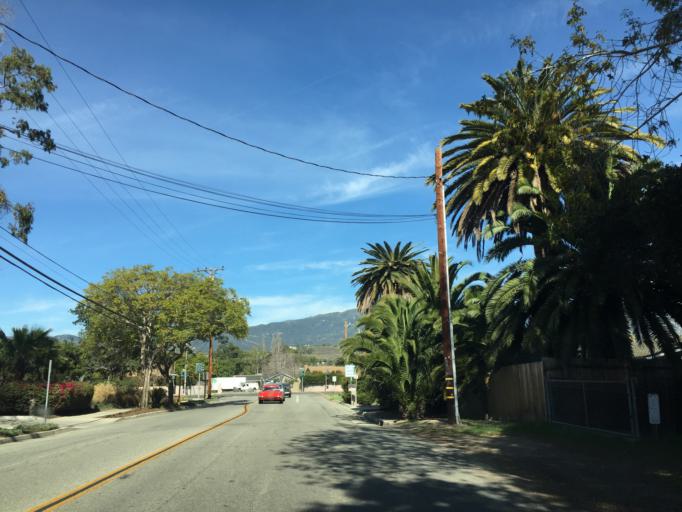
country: US
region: California
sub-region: Santa Barbara County
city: Goleta
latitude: 34.4367
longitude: -119.7838
